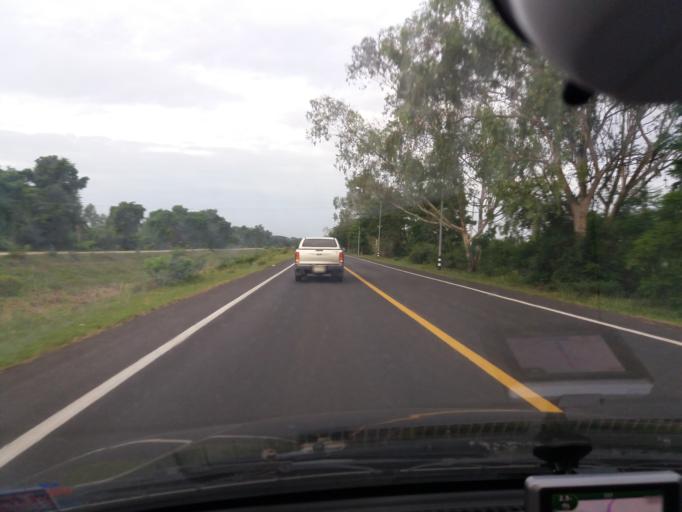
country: TH
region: Suphan Buri
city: Don Chedi
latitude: 14.5284
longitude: 99.9302
